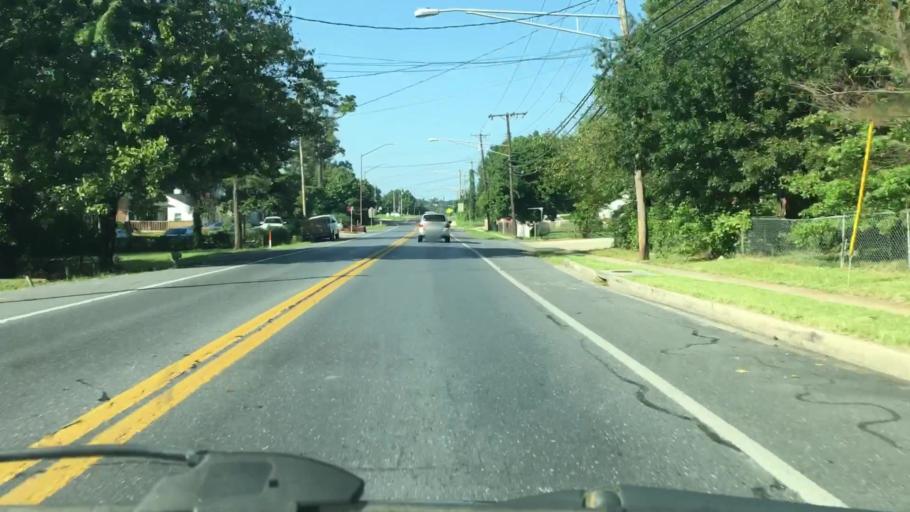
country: US
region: Maryland
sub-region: Prince George's County
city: Lanham
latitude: 38.9667
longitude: -76.8562
